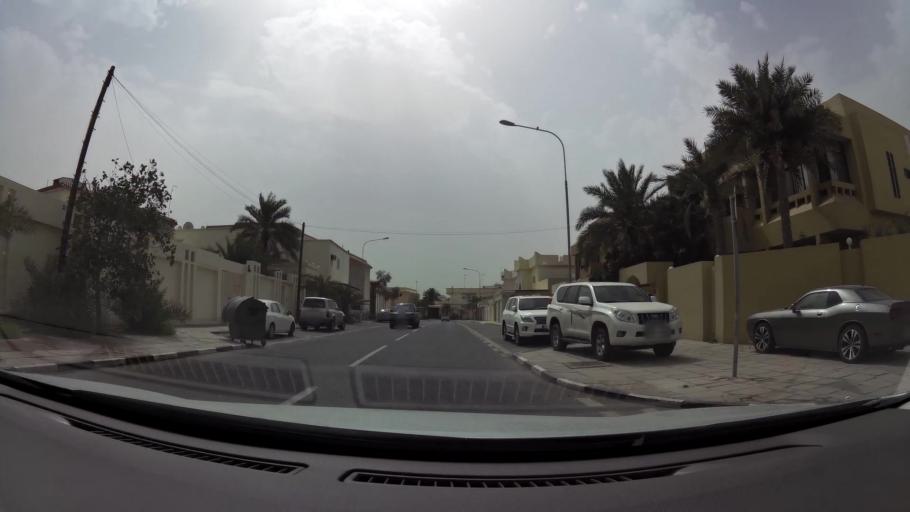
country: QA
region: Baladiyat ad Dawhah
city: Doha
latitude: 25.2606
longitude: 51.5460
